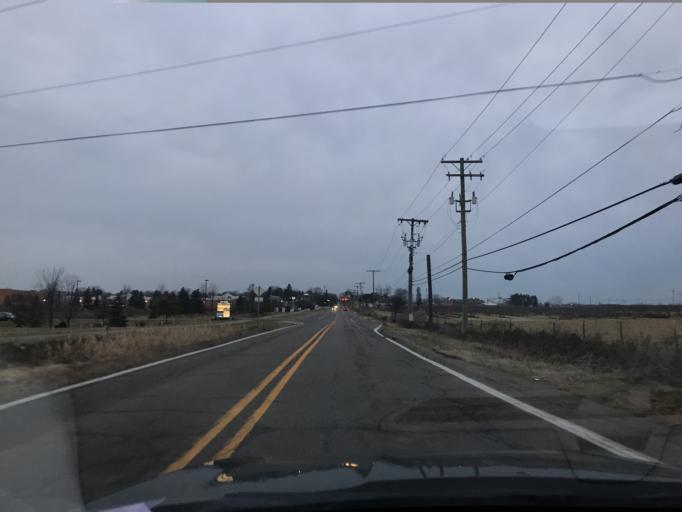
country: US
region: Michigan
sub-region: Macomb County
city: Romeo
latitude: 42.7725
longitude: -83.0125
